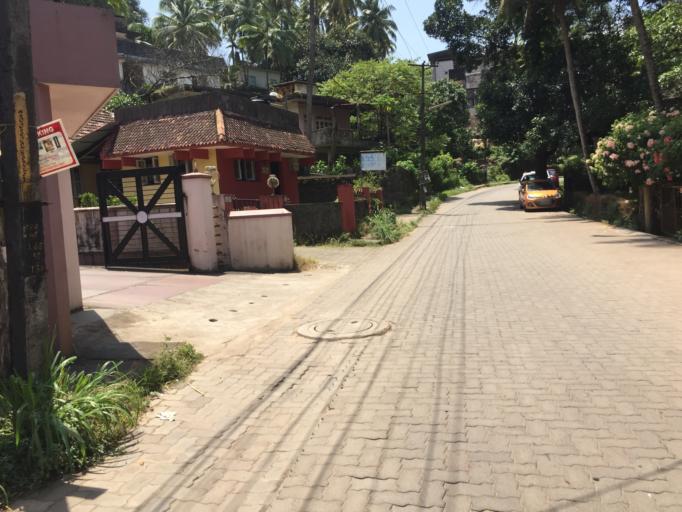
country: IN
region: Karnataka
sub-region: Dakshina Kannada
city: Mangalore
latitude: 12.8754
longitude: 74.8520
